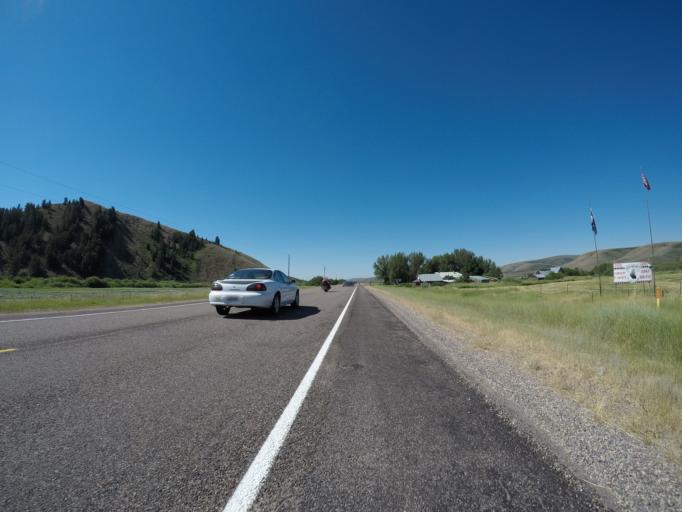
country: US
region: Idaho
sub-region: Bear Lake County
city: Montpelier
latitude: 42.3935
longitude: -111.0512
